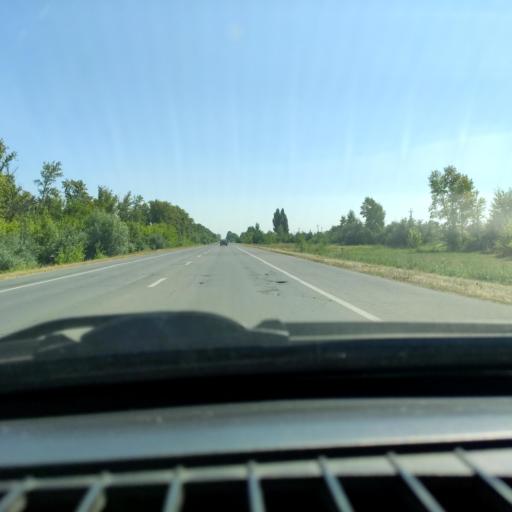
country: RU
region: Samara
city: Tol'yatti
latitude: 53.7066
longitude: 49.4223
